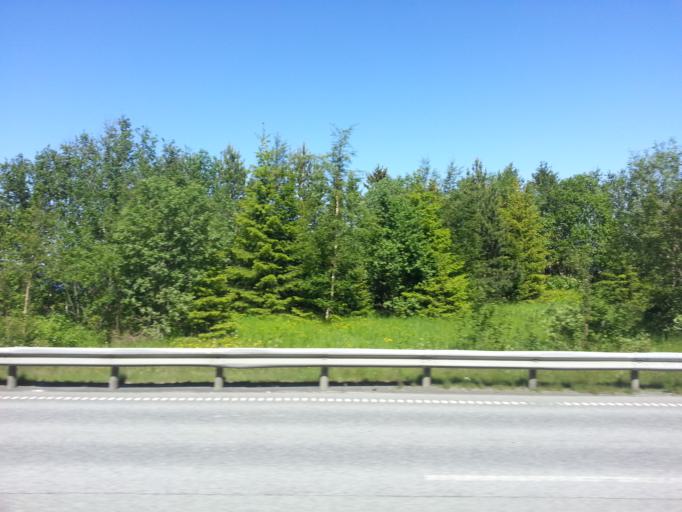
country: NO
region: Sor-Trondelag
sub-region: Malvik
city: Malvik
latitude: 63.4264
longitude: 10.6604
